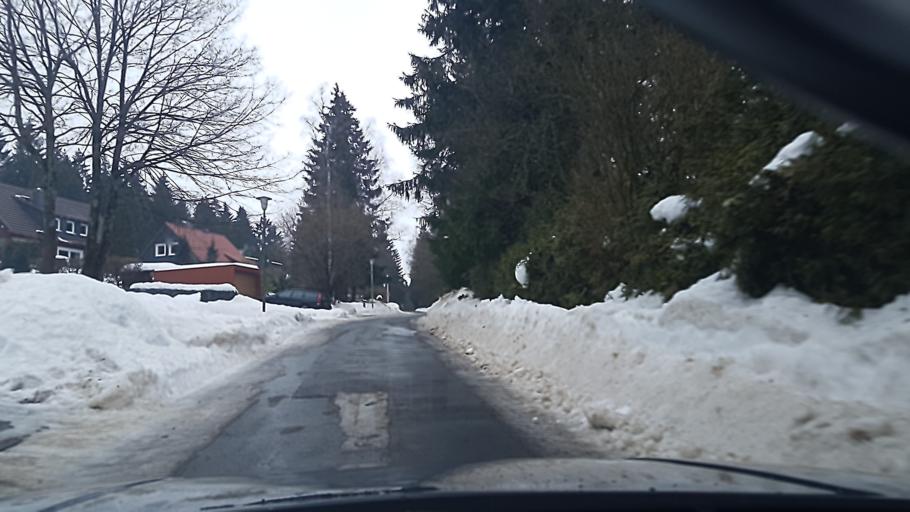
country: DE
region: Lower Saxony
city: Clausthal-Zellerfeld
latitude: 51.8509
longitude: 10.3320
